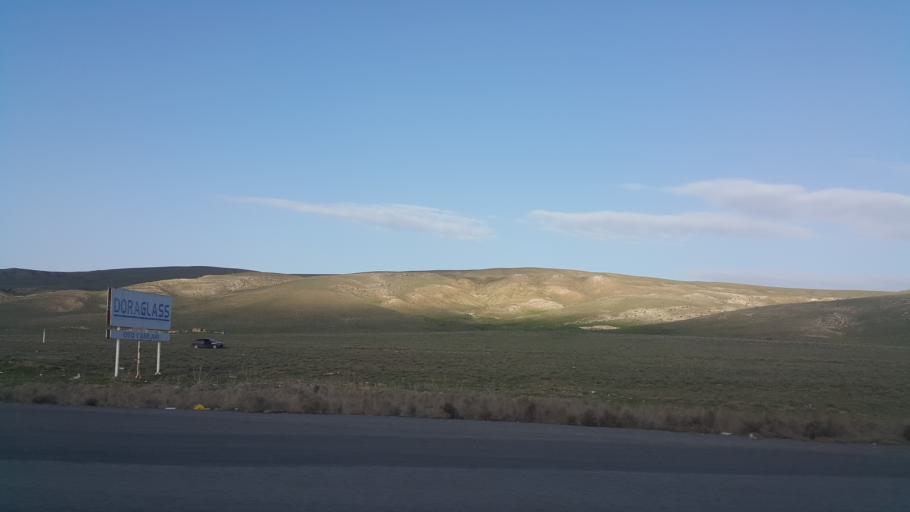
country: TR
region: Konya
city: Kulu
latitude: 39.1312
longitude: 33.3434
